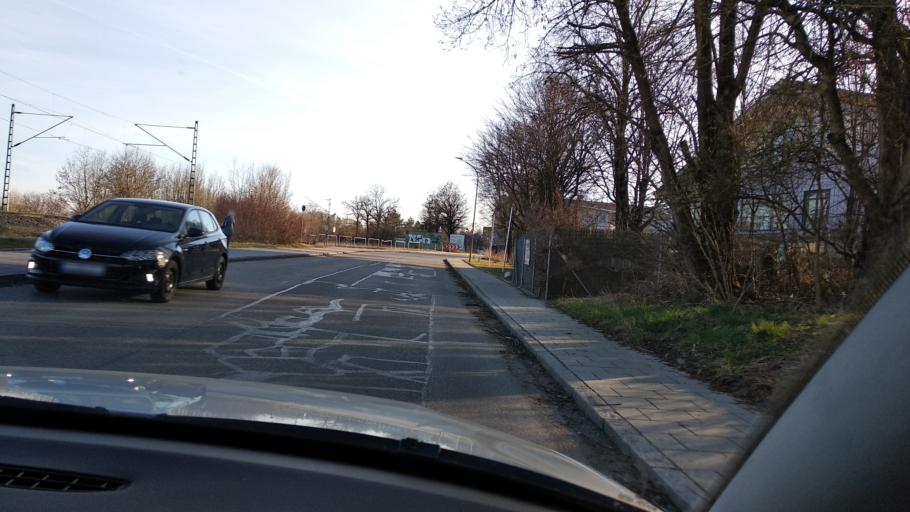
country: DE
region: Bavaria
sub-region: Upper Bavaria
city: Unterhaching
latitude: 48.0571
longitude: 11.6115
